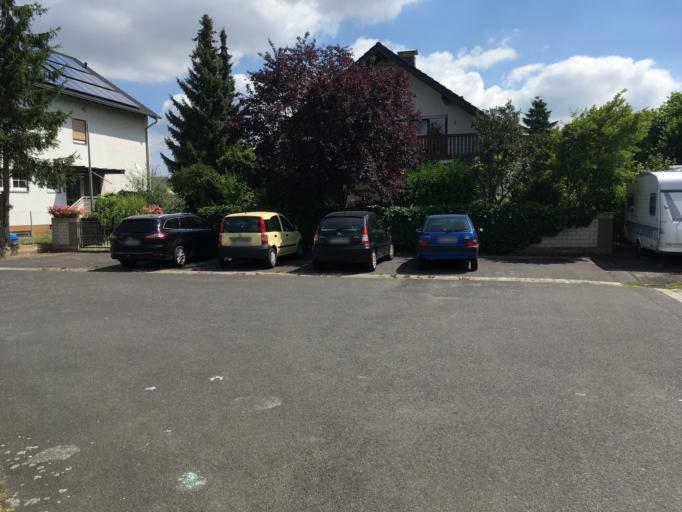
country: DE
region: Hesse
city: Dieburg
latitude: 49.9006
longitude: 8.8524
